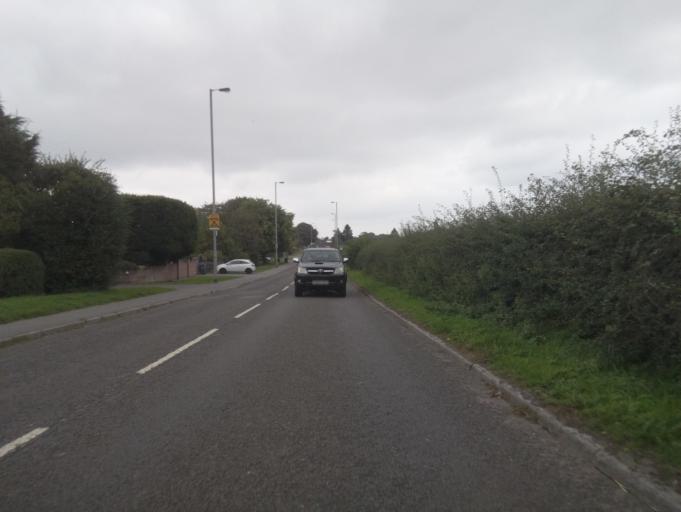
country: GB
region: England
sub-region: Staffordshire
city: Cheddleton
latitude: 53.0268
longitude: -2.0769
